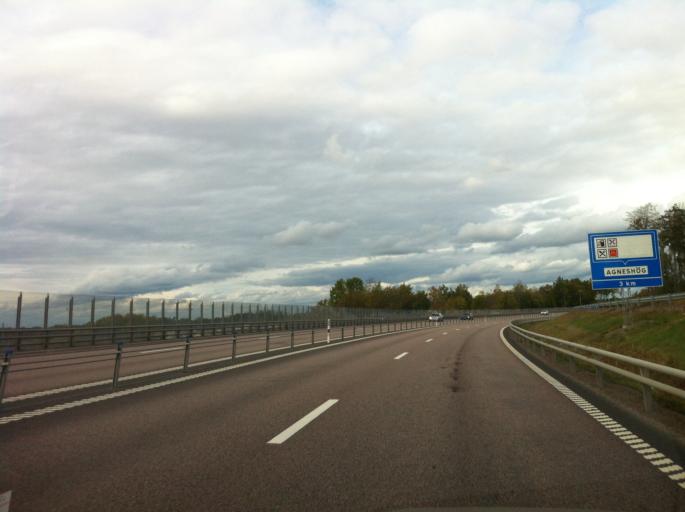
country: SE
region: OEstergoetland
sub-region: Motala Kommun
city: Motala
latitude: 58.5156
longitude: 15.0160
